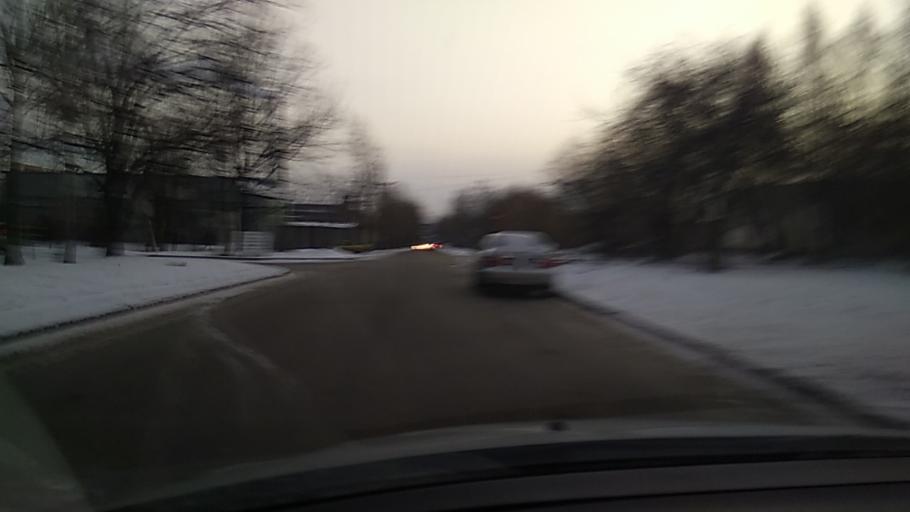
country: RU
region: Sverdlovsk
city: Istok
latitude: 56.7618
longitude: 60.7166
